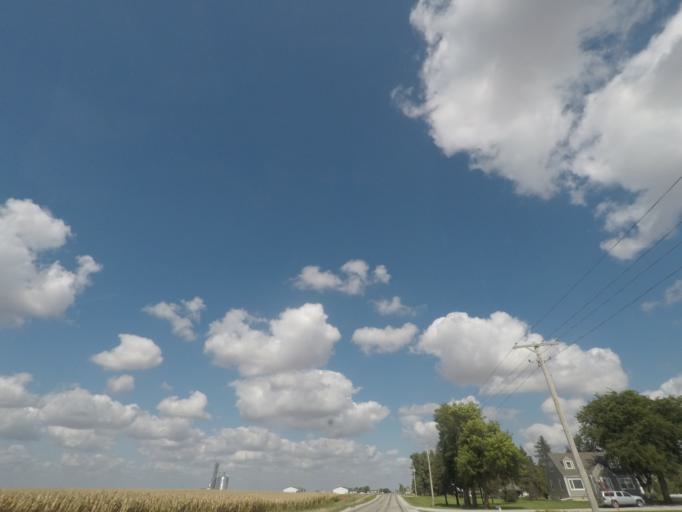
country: US
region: Iowa
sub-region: Story County
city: Nevada
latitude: 42.0433
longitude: -93.4056
